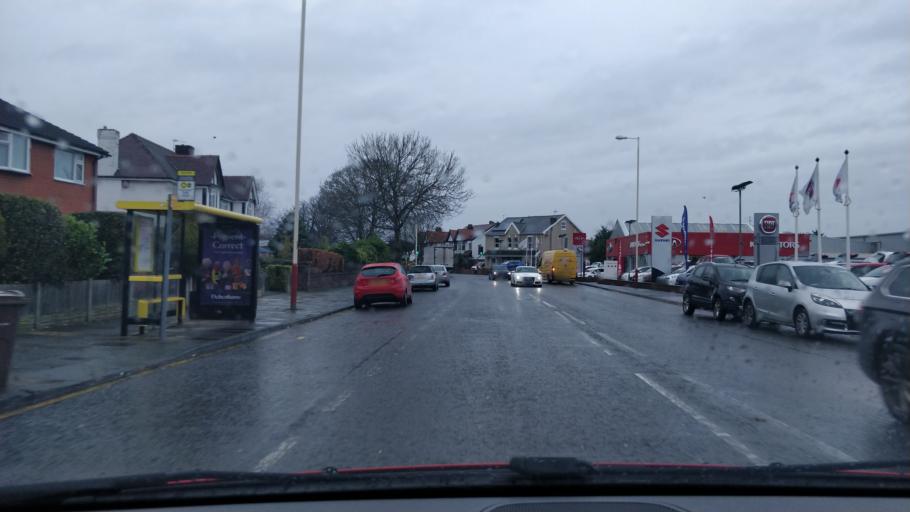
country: GB
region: England
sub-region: Sefton
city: Formby
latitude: 53.5996
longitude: -3.0342
